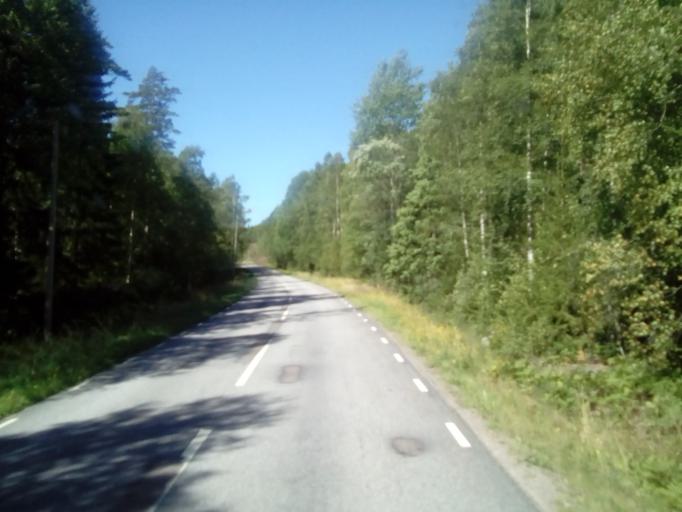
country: SE
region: Kalmar
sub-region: Vimmerby Kommun
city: Sodra Vi
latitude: 57.9083
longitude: 15.9964
